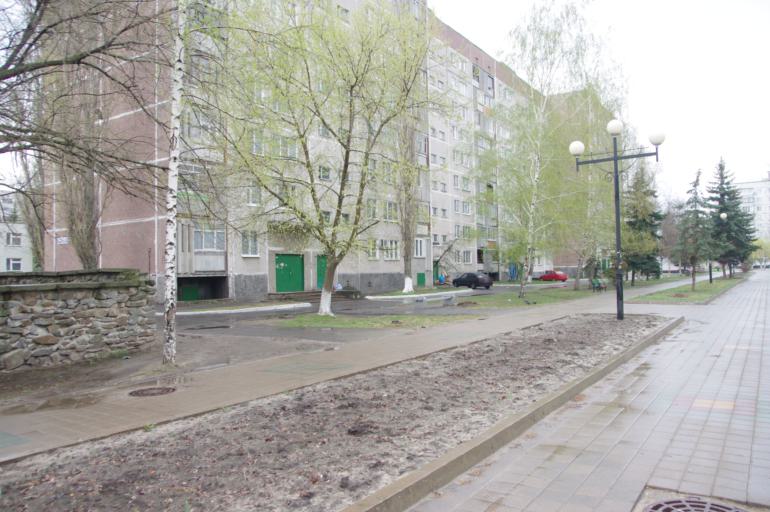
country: RU
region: Kursk
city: Kurchatov
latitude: 51.6557
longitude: 35.6769
